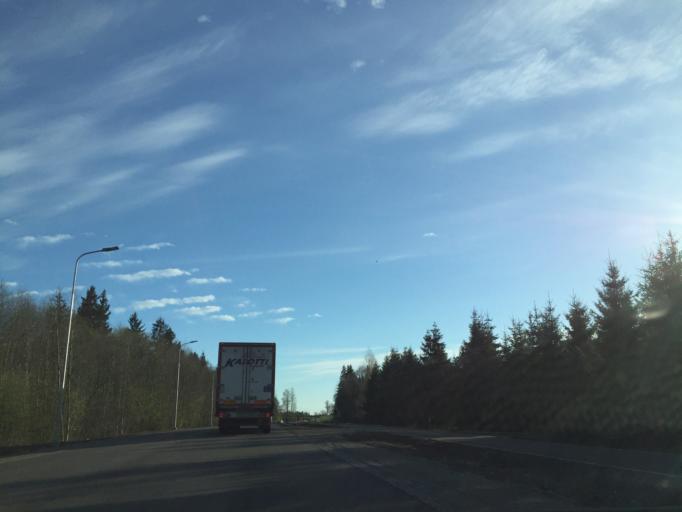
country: LV
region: Valkas Rajons
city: Valka
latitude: 57.7625
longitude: 25.9996
